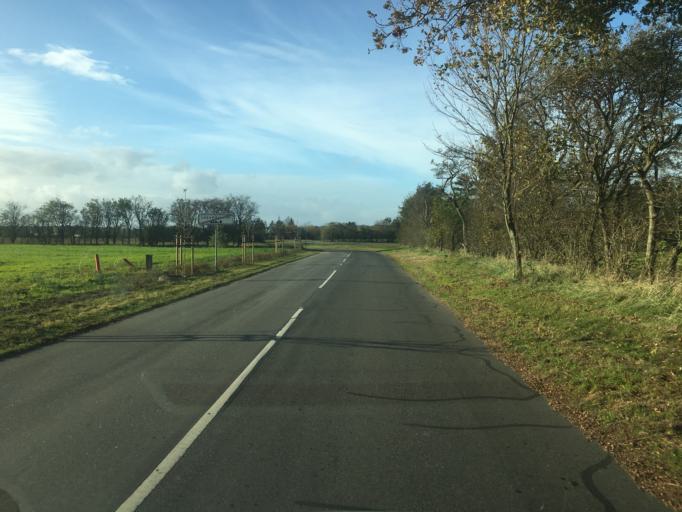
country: DK
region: South Denmark
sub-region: Tonder Kommune
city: Logumkloster
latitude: 55.0709
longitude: 8.9473
